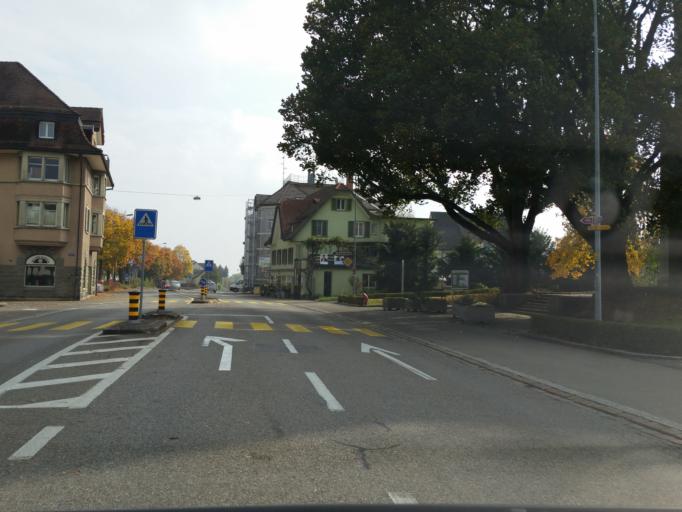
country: CH
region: Thurgau
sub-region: Arbon District
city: Amriswil
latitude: 47.5452
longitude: 9.2973
